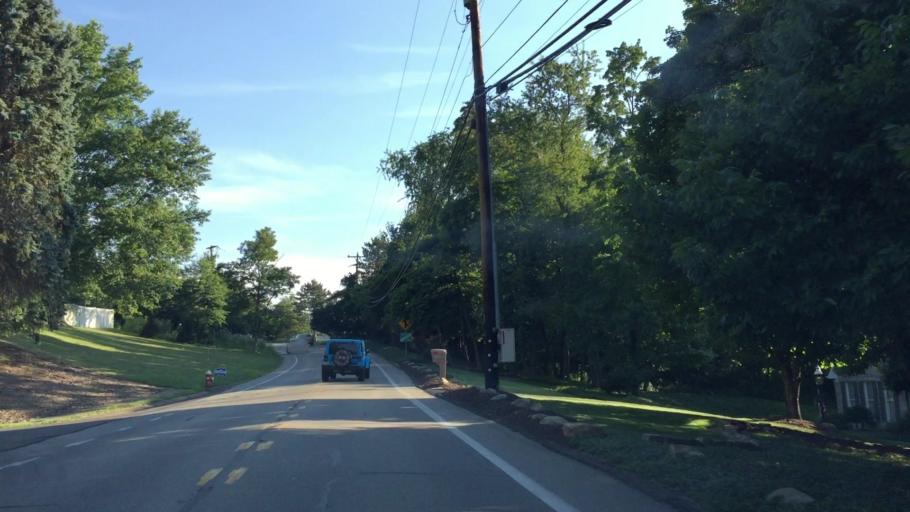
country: US
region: Pennsylvania
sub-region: Allegheny County
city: Franklin Park
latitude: 40.5683
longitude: -80.0778
